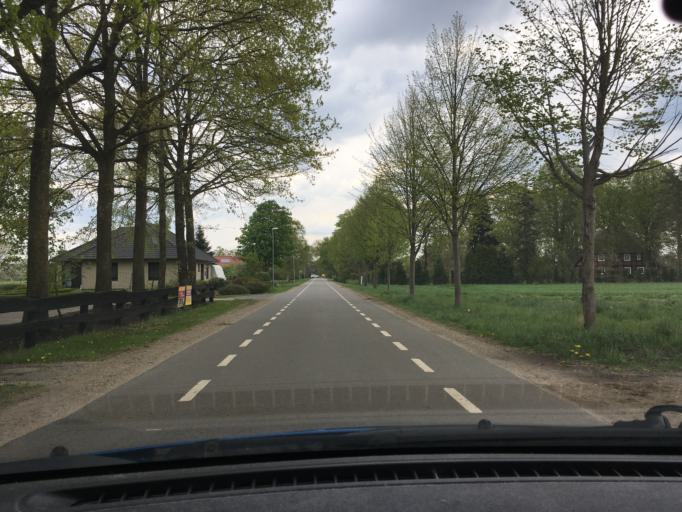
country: DE
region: Lower Saxony
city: Radbruch
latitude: 53.3061
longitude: 10.2769
